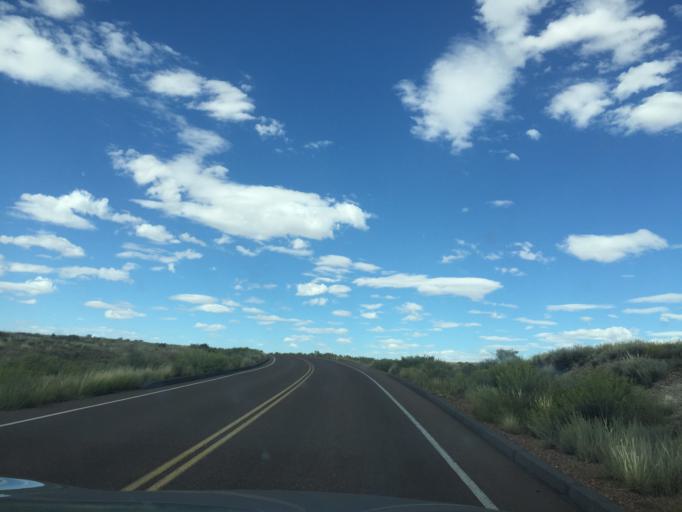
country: US
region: Arizona
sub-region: Navajo County
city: Holbrook
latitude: 34.8433
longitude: -109.8048
